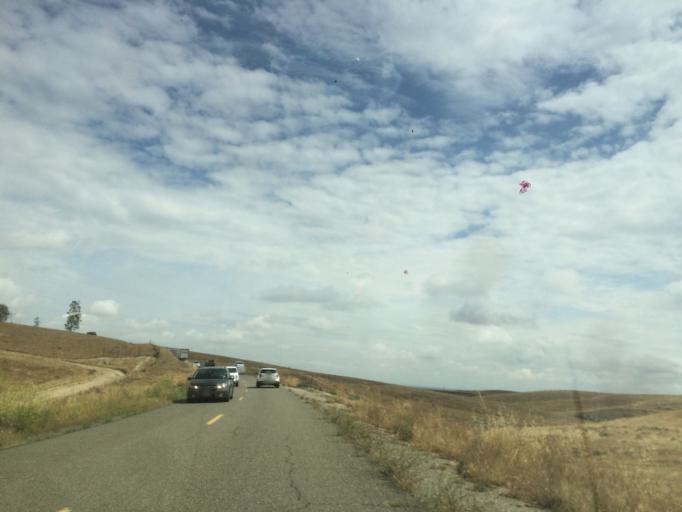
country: US
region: California
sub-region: Fresno County
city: Coalinga
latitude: 36.3242
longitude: -120.3020
